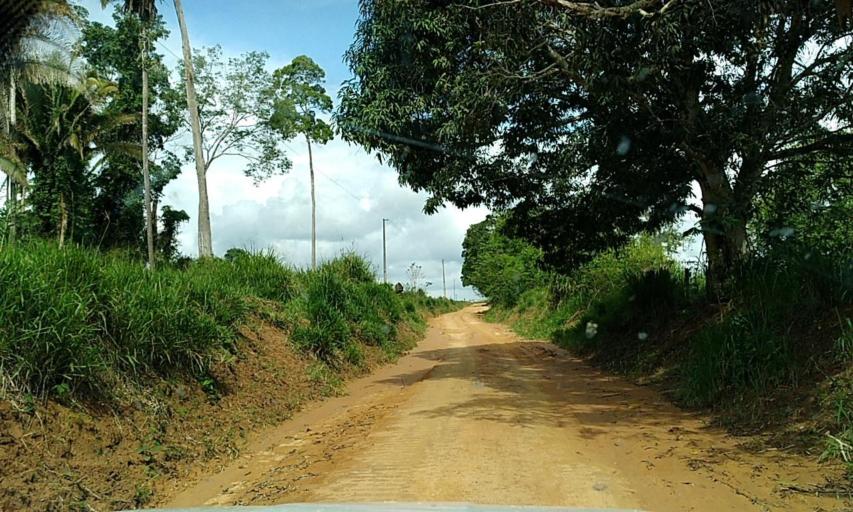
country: BR
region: Para
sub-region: Altamira
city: Altamira
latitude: -3.2368
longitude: -52.7451
